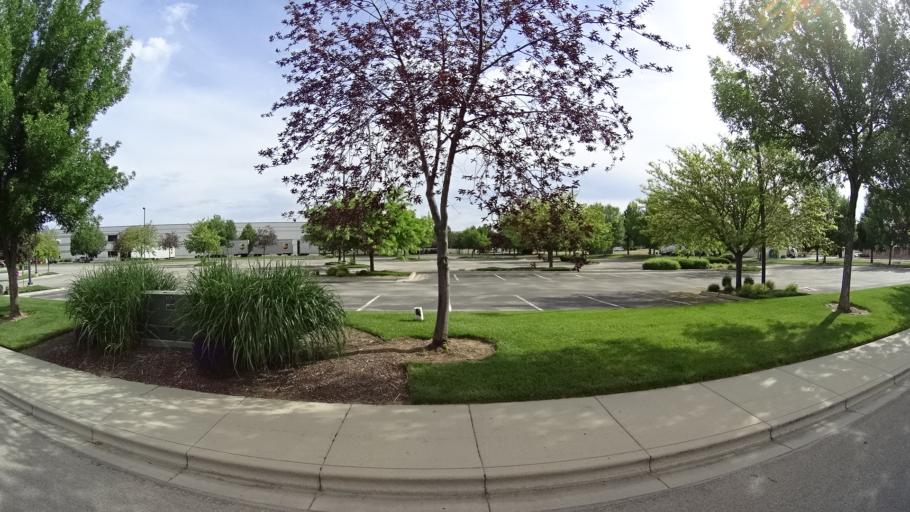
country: US
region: Idaho
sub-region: Ada County
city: Meridian
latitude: 43.5838
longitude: -116.3503
